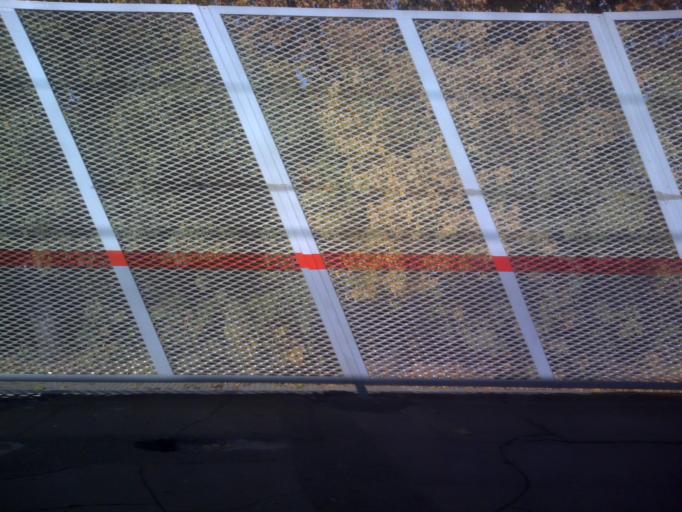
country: RU
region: Moskovskaya
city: Biryulevo Zapadnoye
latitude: 55.6037
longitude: 37.6326
